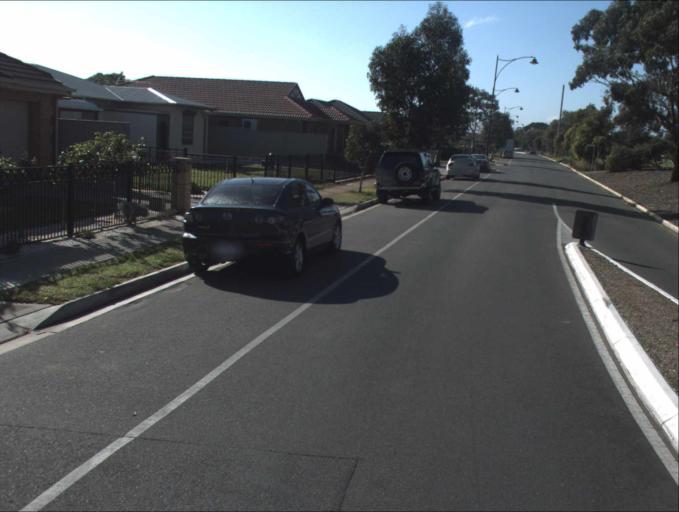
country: AU
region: South Australia
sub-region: Charles Sturt
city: Woodville North
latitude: -34.8561
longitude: 138.5495
